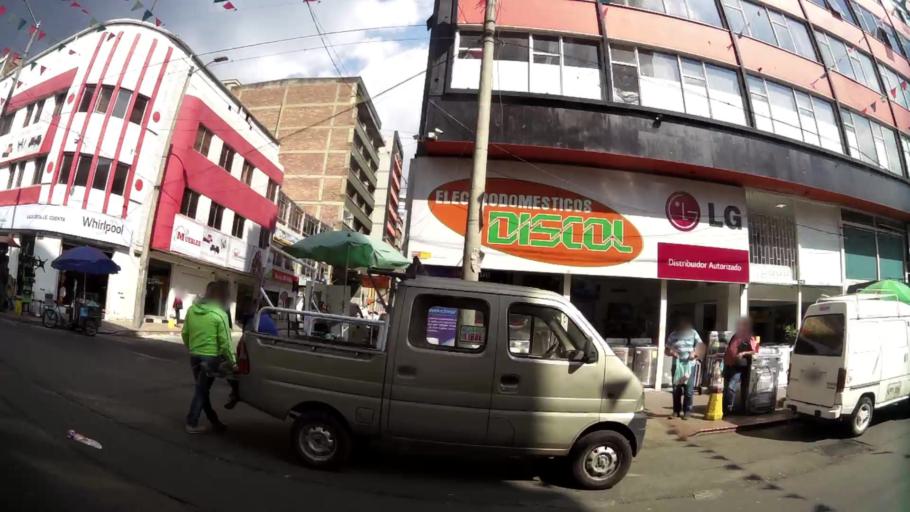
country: CO
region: Bogota D.C.
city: Bogota
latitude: 4.6054
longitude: -74.0772
